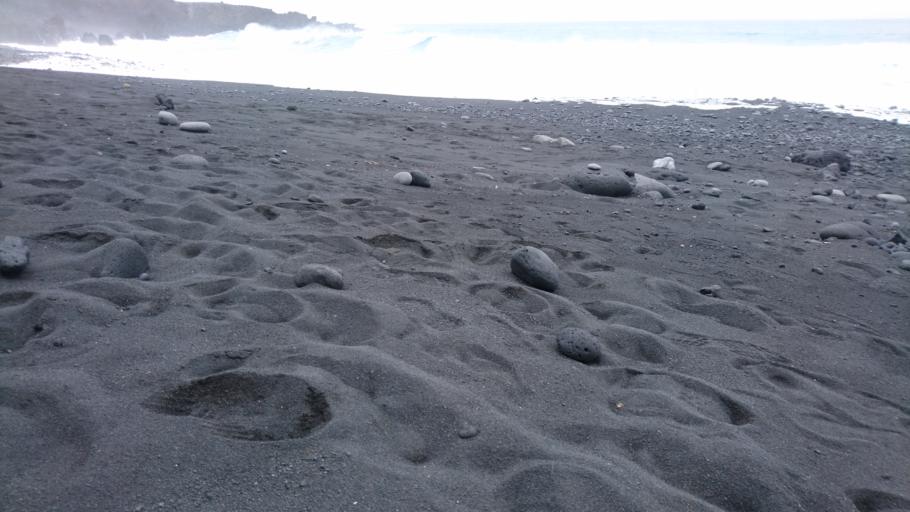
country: ES
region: Canary Islands
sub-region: Provincia de Santa Cruz de Tenerife
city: Tazacorte
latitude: 28.6017
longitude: -17.9234
